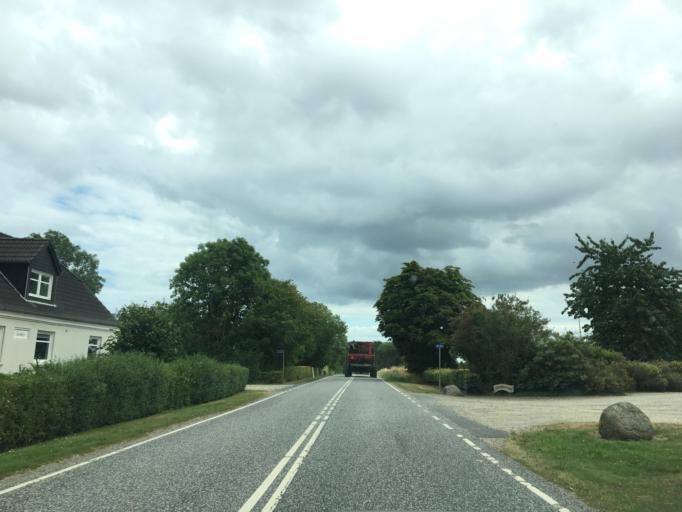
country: DK
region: South Denmark
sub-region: Nyborg Kommune
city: Ullerslev
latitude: 55.3191
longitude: 10.6988
